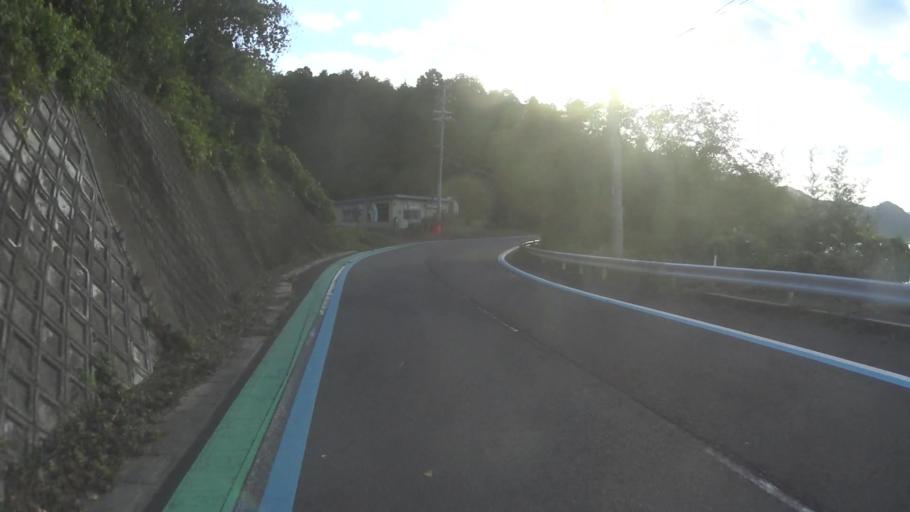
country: JP
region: Kyoto
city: Maizuru
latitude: 35.4249
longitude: 135.2508
